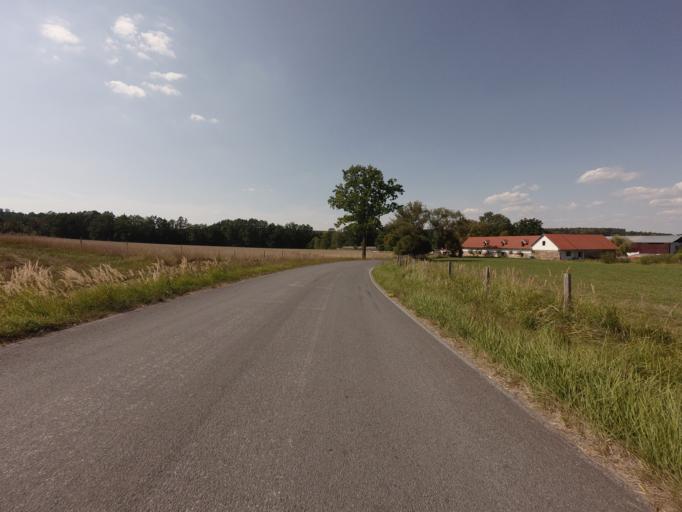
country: CZ
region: Jihocesky
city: Tyn nad Vltavou
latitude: 49.1468
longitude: 14.4450
